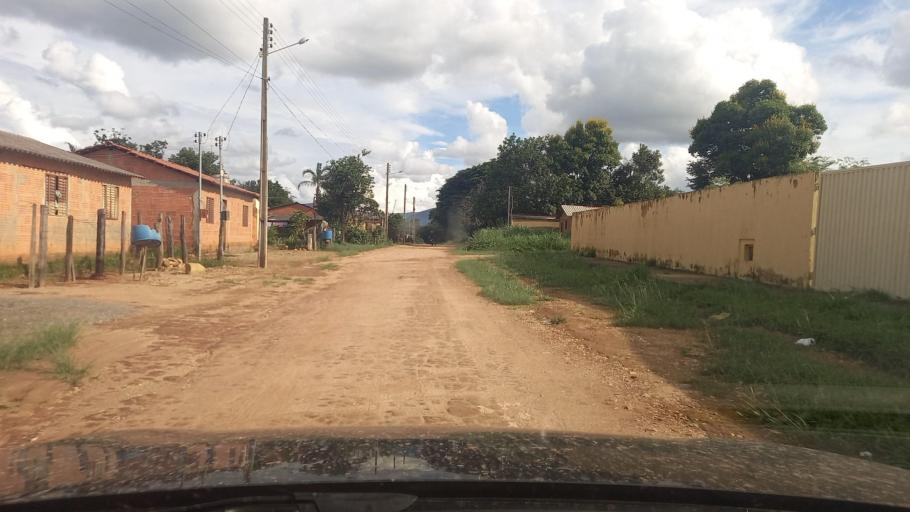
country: BR
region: Goias
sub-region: Cavalcante
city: Cavalcante
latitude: -13.8004
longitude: -47.4460
